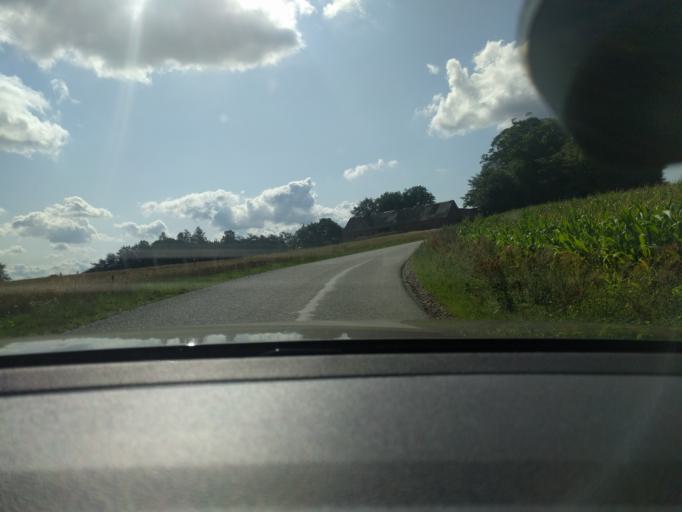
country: DK
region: Central Jutland
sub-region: Viborg Kommune
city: Viborg
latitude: 56.5252
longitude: 9.3512
